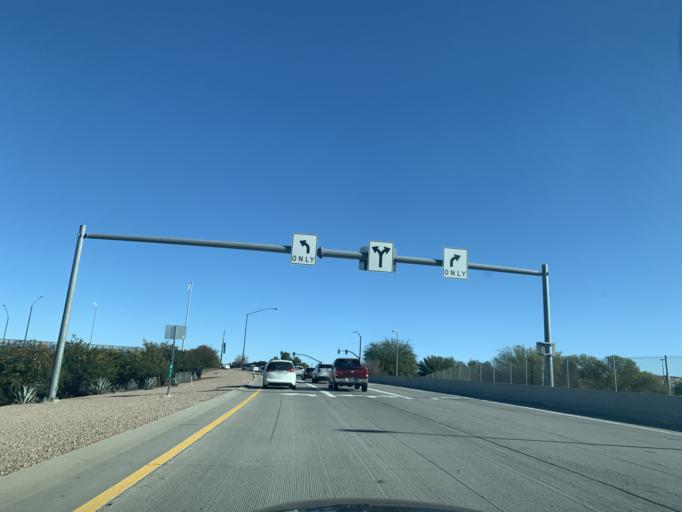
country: US
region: Arizona
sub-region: Maricopa County
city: Gilbert
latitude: 33.2958
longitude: -111.7422
